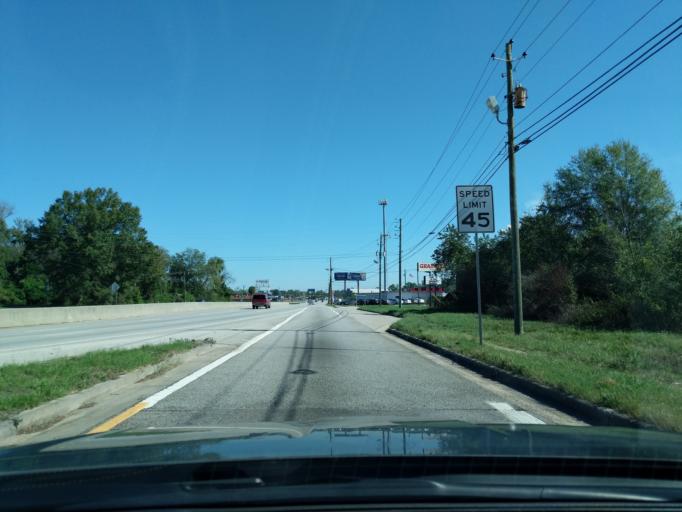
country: US
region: Georgia
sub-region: Richmond County
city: Augusta
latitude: 33.4373
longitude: -82.0041
